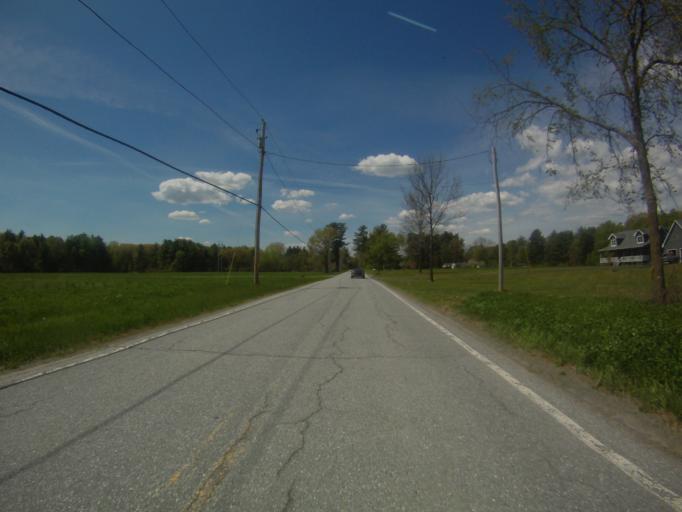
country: US
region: New York
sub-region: Essex County
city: Port Henry
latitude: 43.9621
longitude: -73.4237
